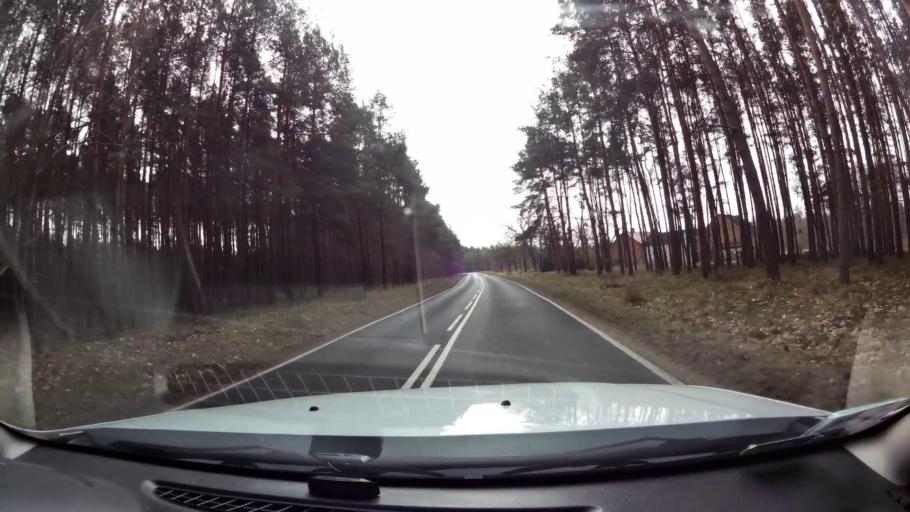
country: PL
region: West Pomeranian Voivodeship
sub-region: Powiat mysliborski
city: Debno
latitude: 52.7616
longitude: 14.6794
